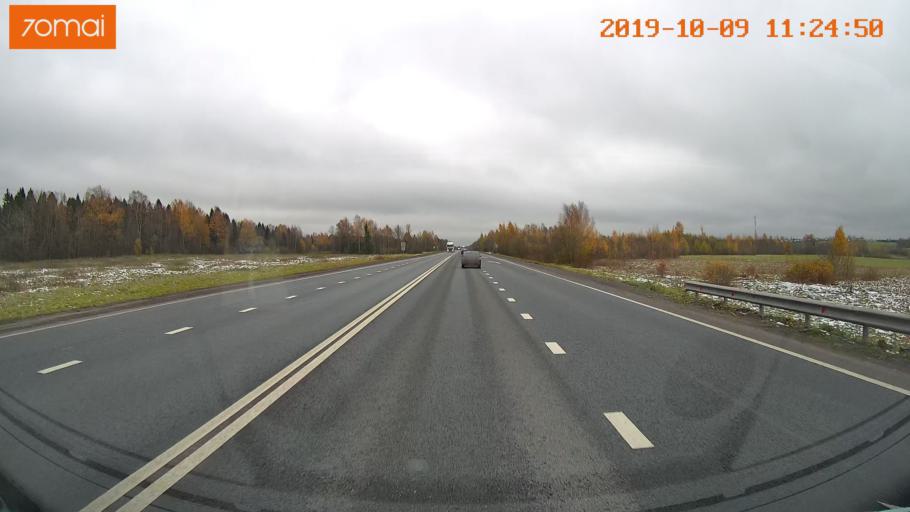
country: RU
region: Vologda
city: Vologda
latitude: 59.1076
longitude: 39.9843
